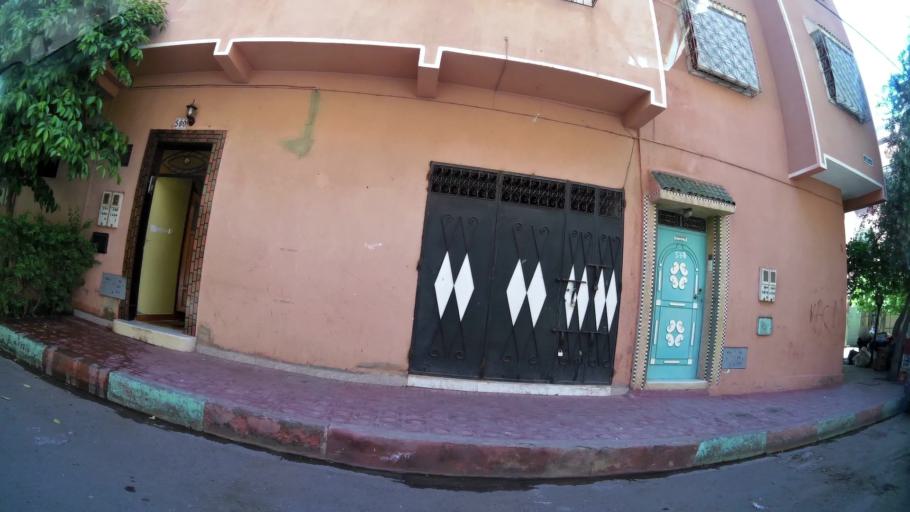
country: MA
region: Marrakech-Tensift-Al Haouz
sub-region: Marrakech
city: Marrakesh
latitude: 31.6433
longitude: -8.0663
